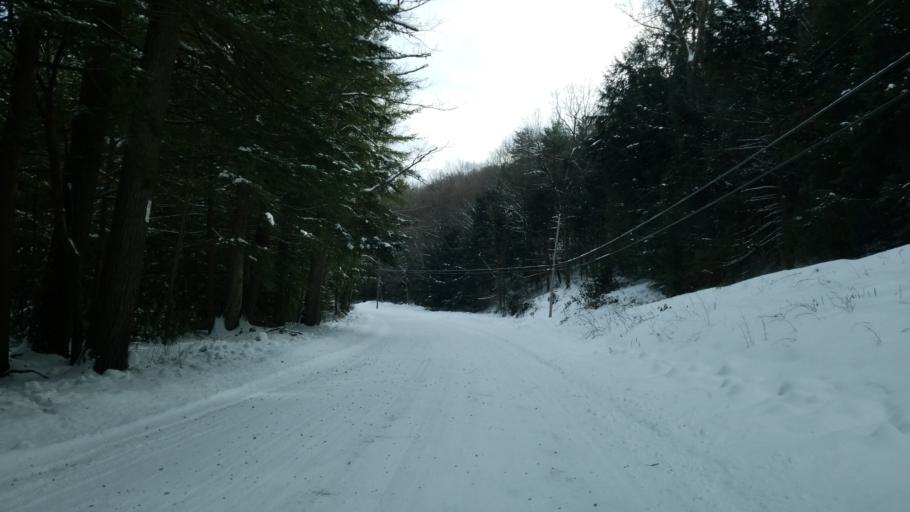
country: US
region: Pennsylvania
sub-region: Clearfield County
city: Clearfield
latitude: 41.0518
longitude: -78.4714
